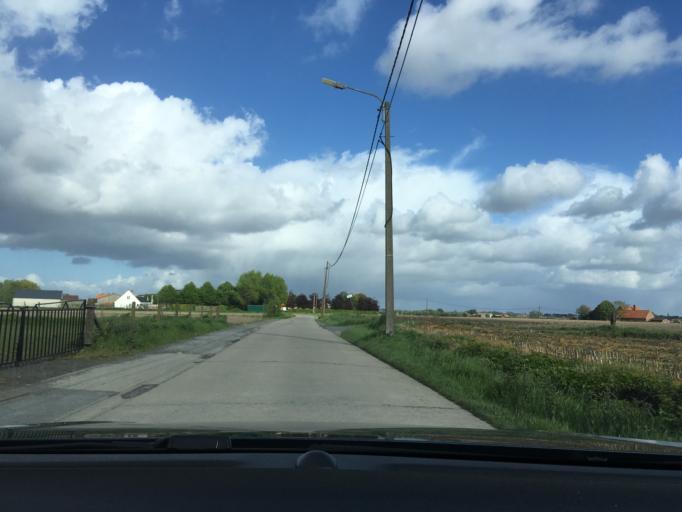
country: BE
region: Flanders
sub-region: Provincie West-Vlaanderen
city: Hooglede
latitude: 50.9994
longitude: 3.0591
